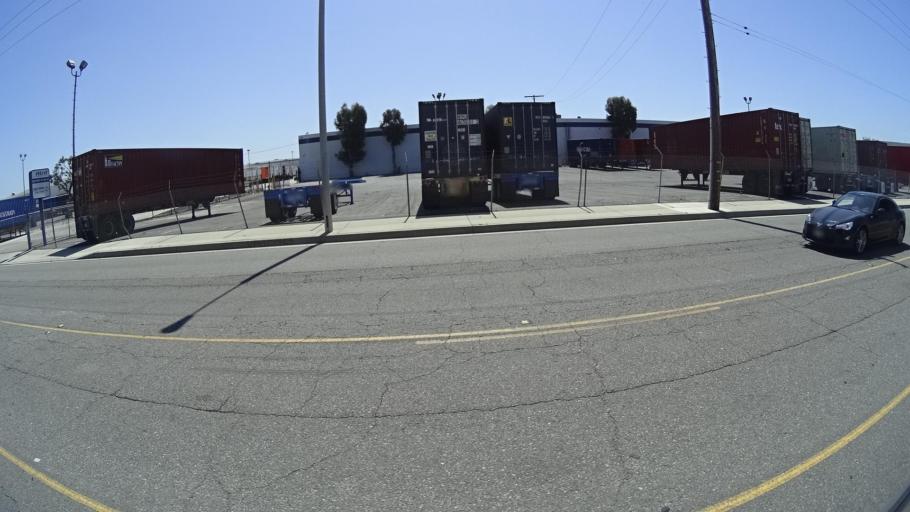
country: US
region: California
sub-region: Los Angeles County
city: Avocado Heights
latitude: 34.0562
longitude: -117.9997
